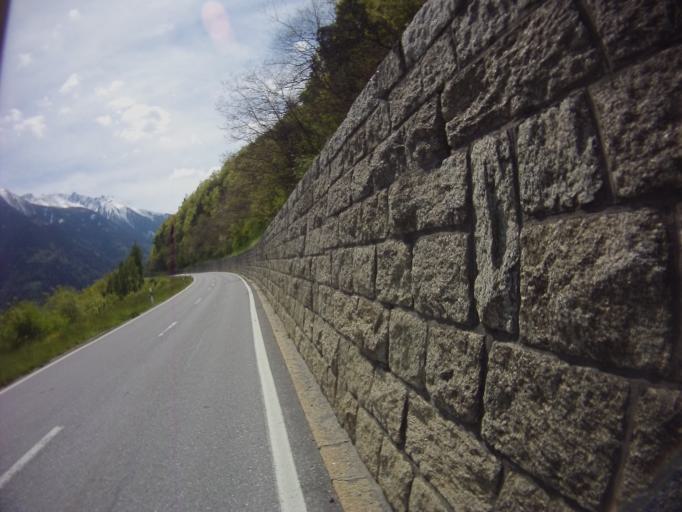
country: CH
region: Valais
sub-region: Martigny District
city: Martigny-Combe
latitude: 46.0909
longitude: 7.0469
